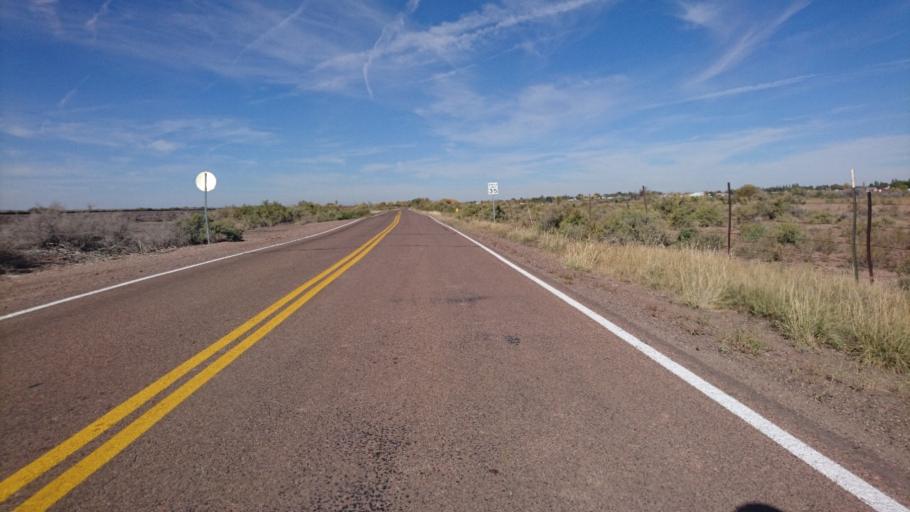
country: US
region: Arizona
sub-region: Navajo County
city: Joseph City
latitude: 34.9452
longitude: -110.3248
